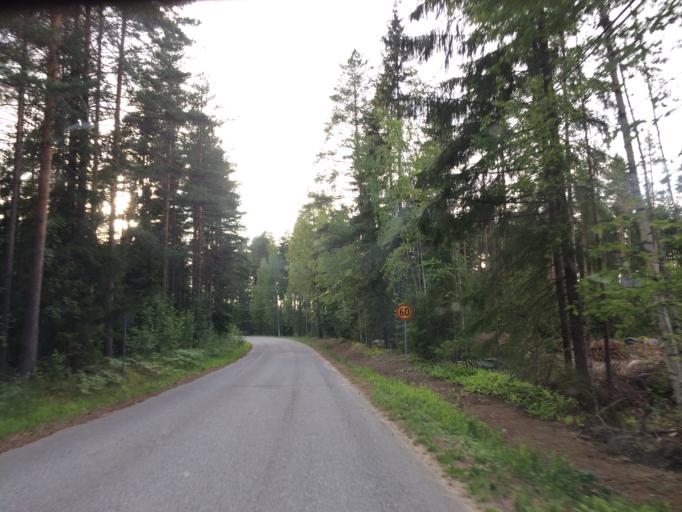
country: FI
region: Haeme
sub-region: Haemeenlinna
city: Tervakoski
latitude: 60.8540
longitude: 24.6180
